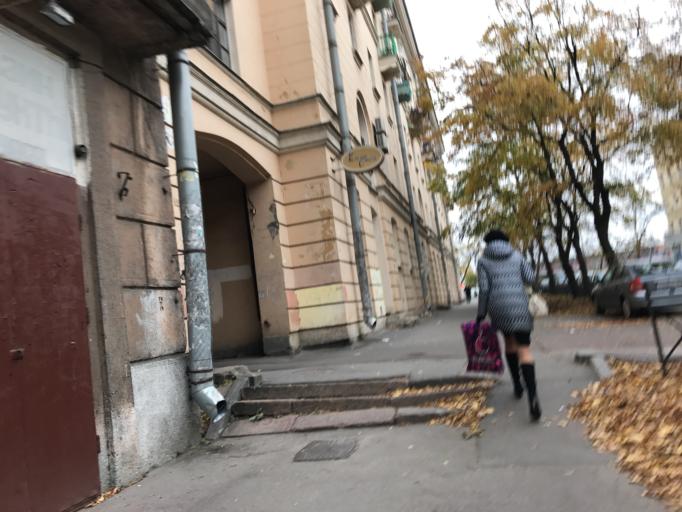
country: RU
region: St.-Petersburg
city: Obukhovo
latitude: 59.8983
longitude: 30.4289
